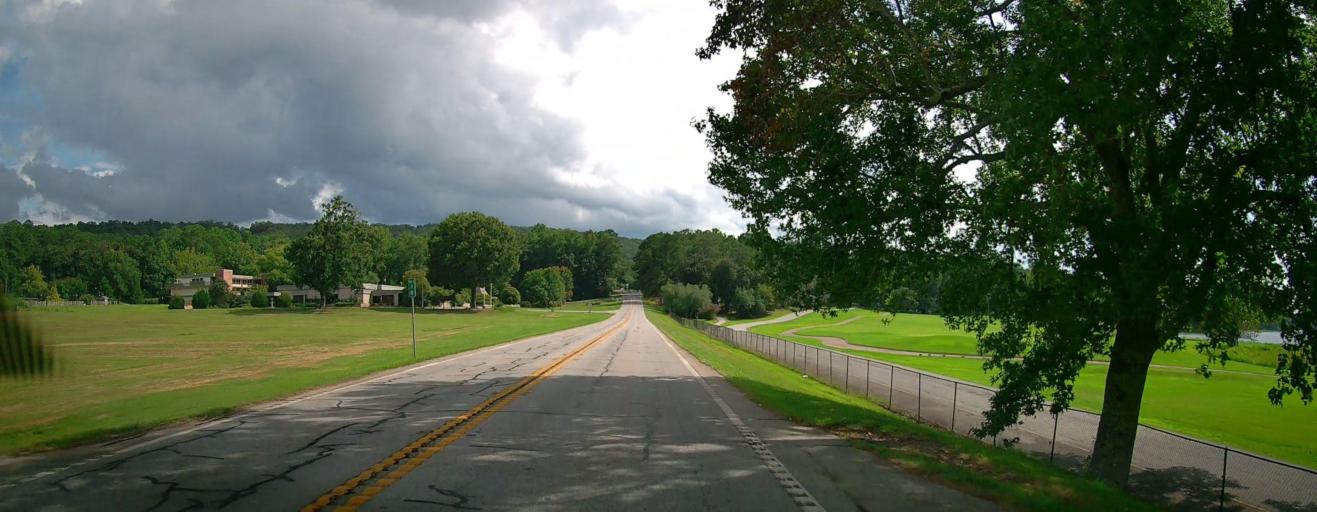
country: US
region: Georgia
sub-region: Harris County
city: Pine Mountain
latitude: 32.8319
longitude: -84.8437
